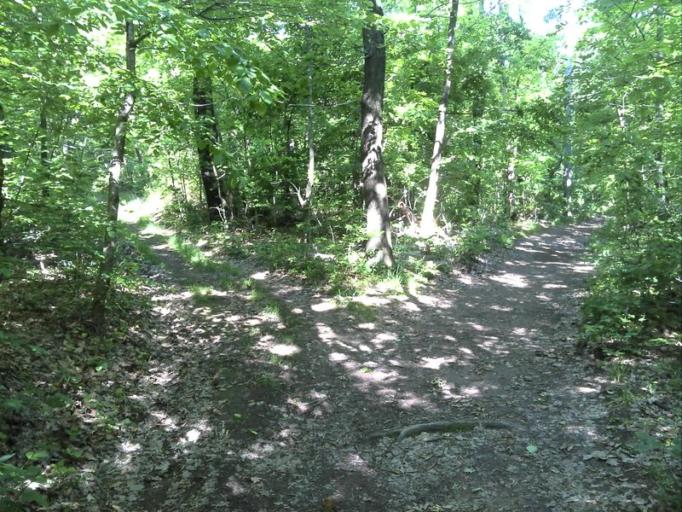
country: HU
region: Baranya
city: Pellerd
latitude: 46.0895
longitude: 18.1706
